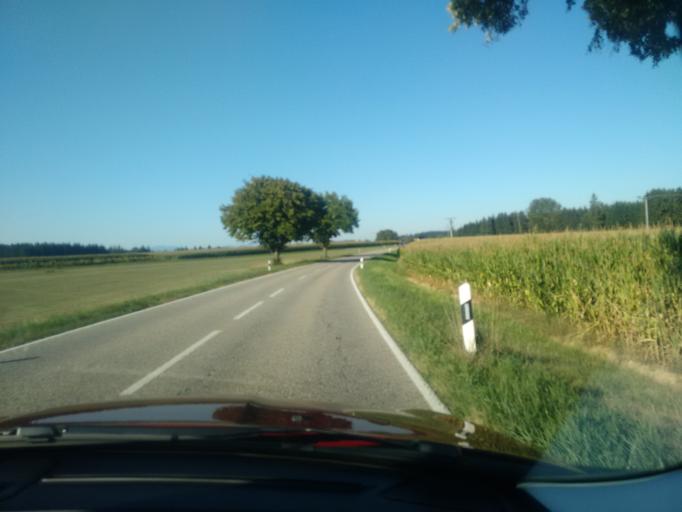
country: DE
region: Bavaria
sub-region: Upper Bavaria
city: Kirchweidach
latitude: 48.0758
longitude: 12.6241
